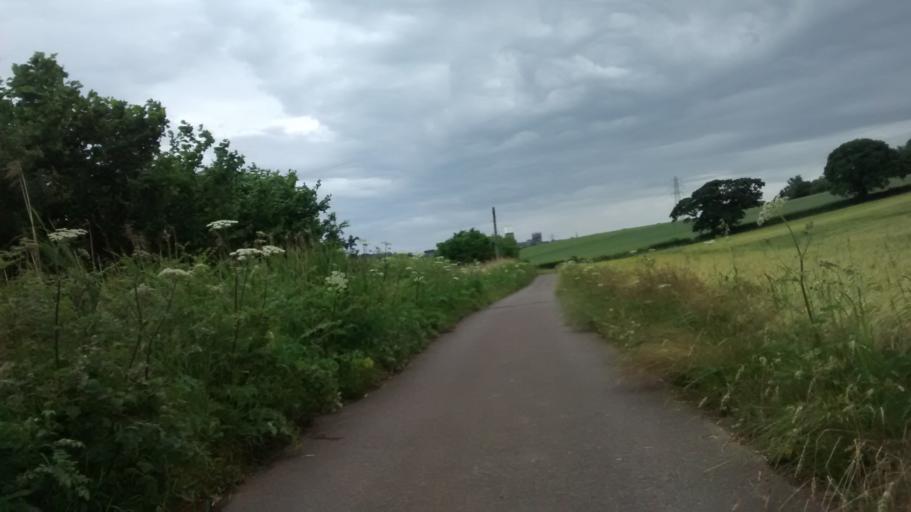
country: GB
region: England
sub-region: County Durham
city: Durham
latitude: 54.7899
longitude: -1.5643
